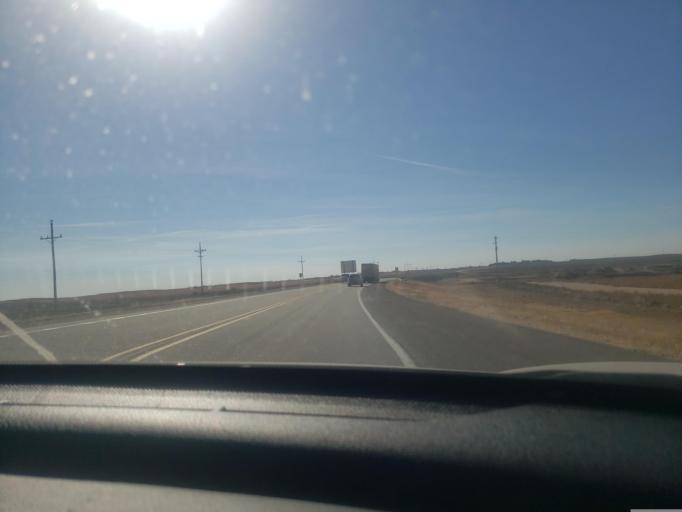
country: US
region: Kansas
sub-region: Finney County
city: Garden City
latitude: 37.9532
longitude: -100.8411
